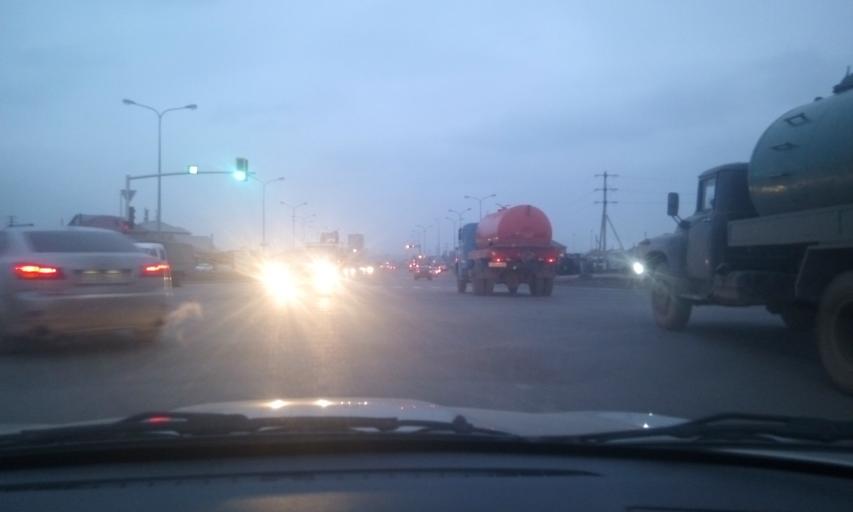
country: KZ
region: Astana Qalasy
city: Astana
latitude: 51.1371
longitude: 71.5217
